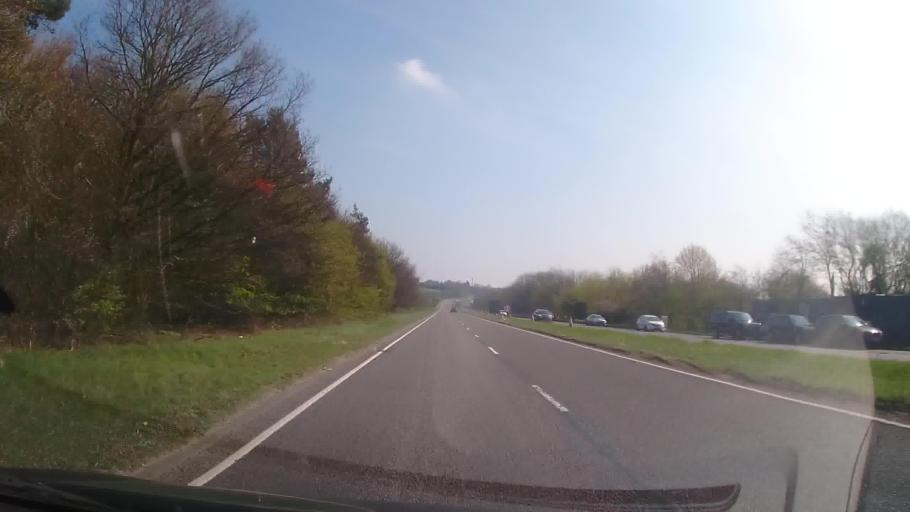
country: GB
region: England
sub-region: Leicestershire
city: Markfield
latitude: 52.6907
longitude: -1.2741
